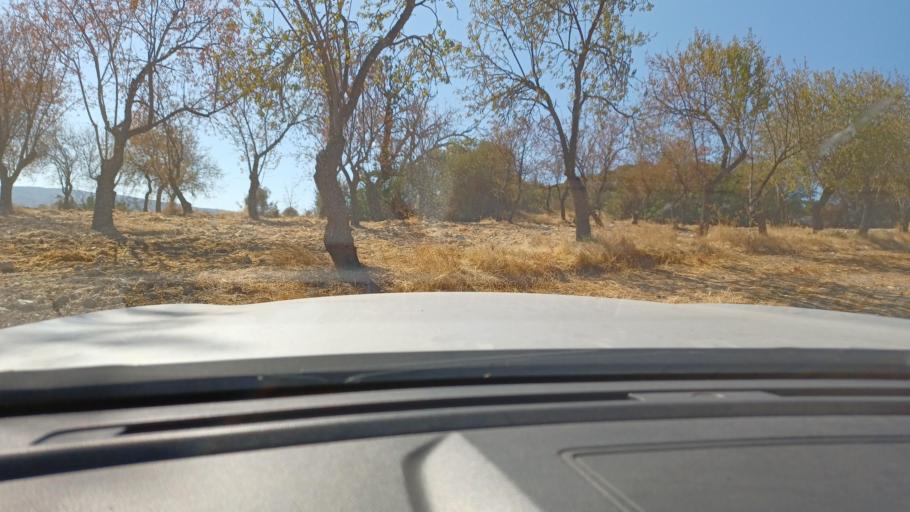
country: CY
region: Pafos
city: Polis
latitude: 34.9689
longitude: 32.5097
